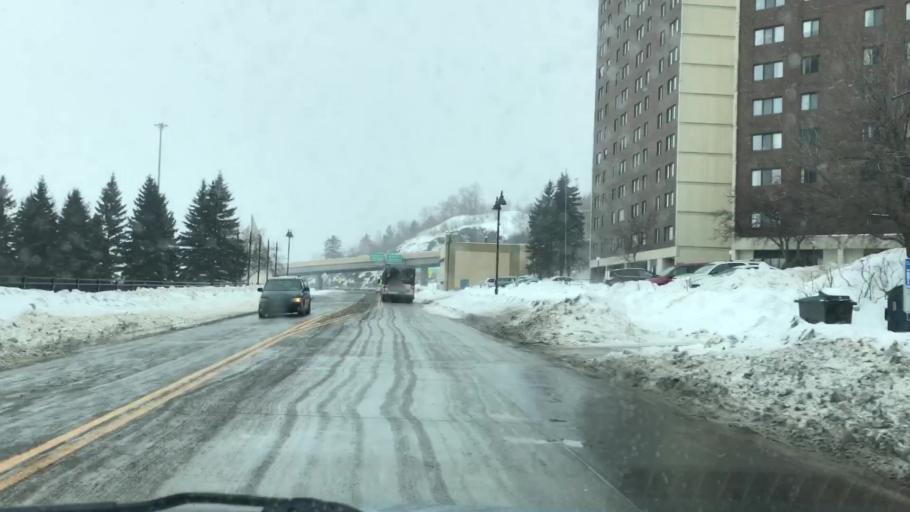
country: US
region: Minnesota
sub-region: Saint Louis County
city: Duluth
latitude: 46.7808
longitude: -92.1062
